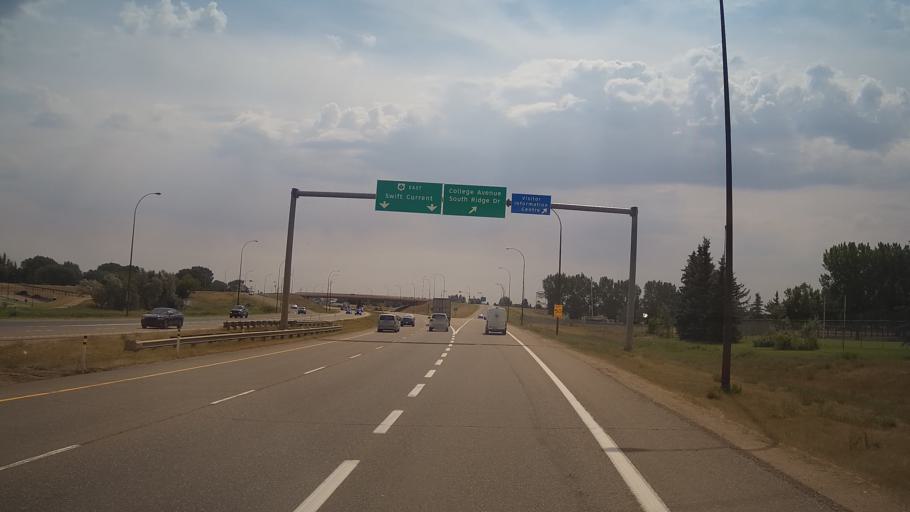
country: CA
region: Alberta
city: Medicine Hat
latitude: 50.0146
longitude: -110.6878
